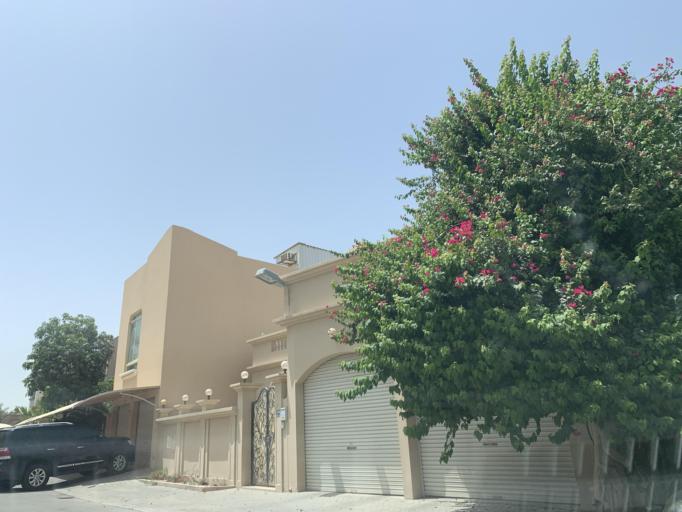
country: BH
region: Northern
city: Madinat `Isa
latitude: 26.1621
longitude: 50.5770
